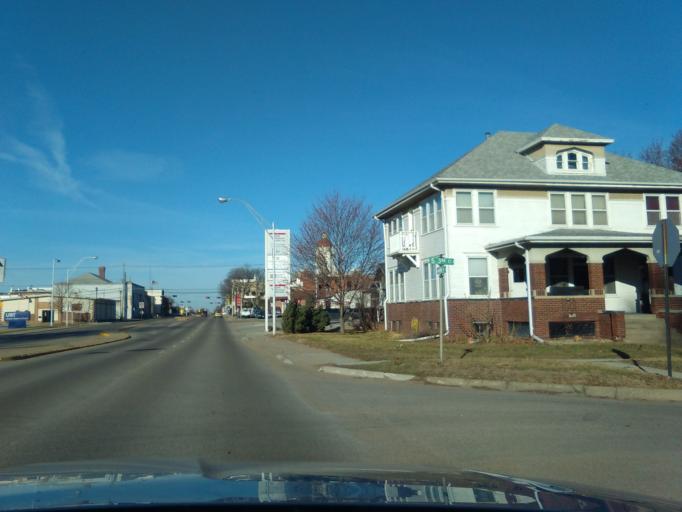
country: US
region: Nebraska
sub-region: Seward County
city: Seward
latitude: 40.9070
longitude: -97.0954
